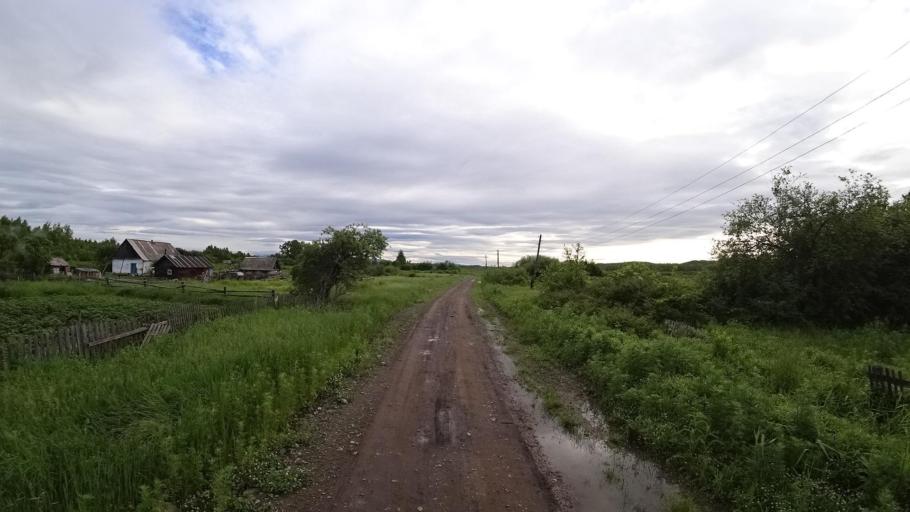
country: RU
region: Khabarovsk Krai
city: Amursk
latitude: 49.8836
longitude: 136.1278
